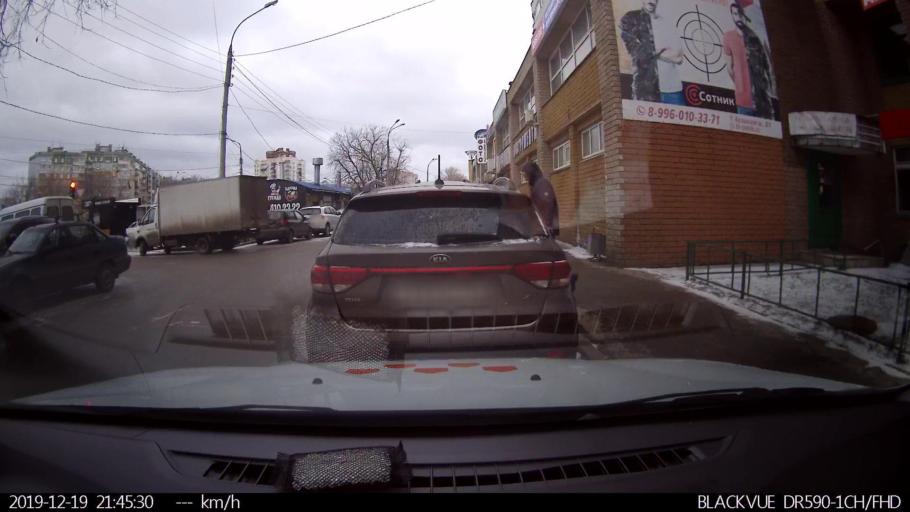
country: RU
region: Nizjnij Novgorod
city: Bor
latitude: 56.4029
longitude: 44.0609
